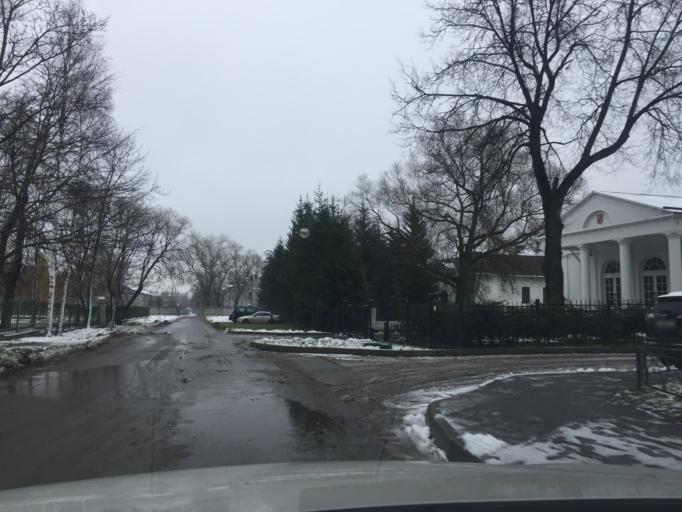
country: RU
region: St.-Petersburg
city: Pushkin
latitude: 59.7041
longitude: 30.3943
